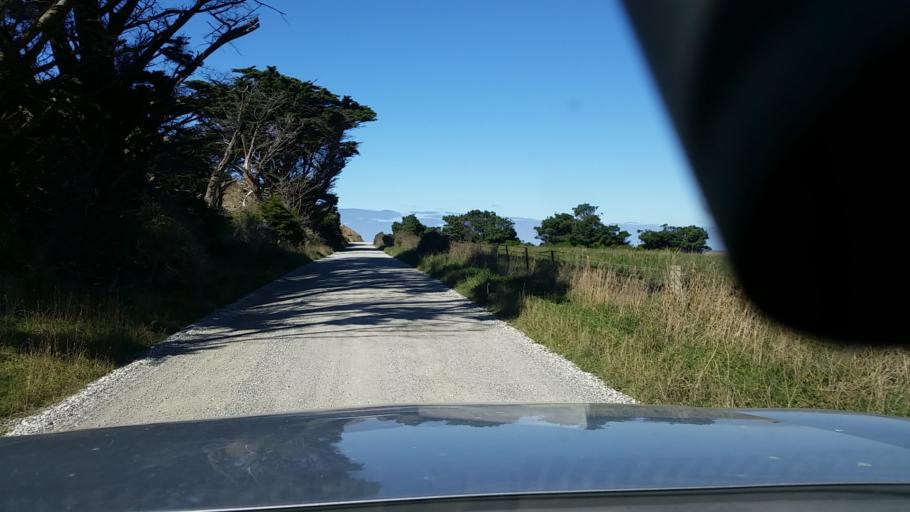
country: NZ
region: Marlborough
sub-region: Marlborough District
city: Blenheim
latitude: -41.8422
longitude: 174.1804
